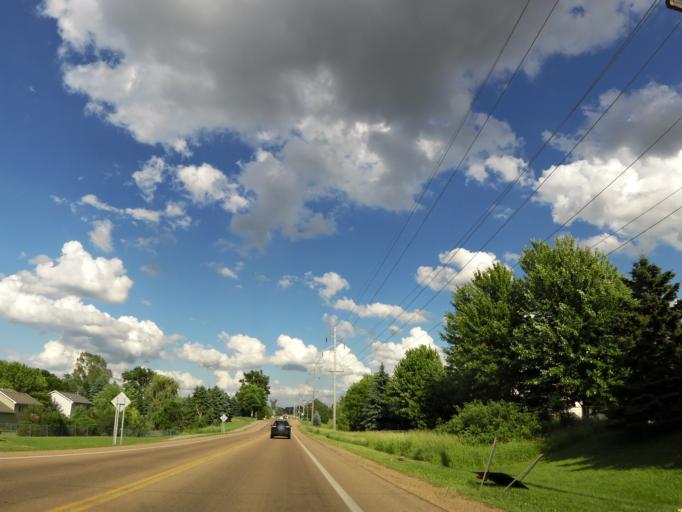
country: US
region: Minnesota
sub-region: Carver County
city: Waconia
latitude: 44.8406
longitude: -93.8072
